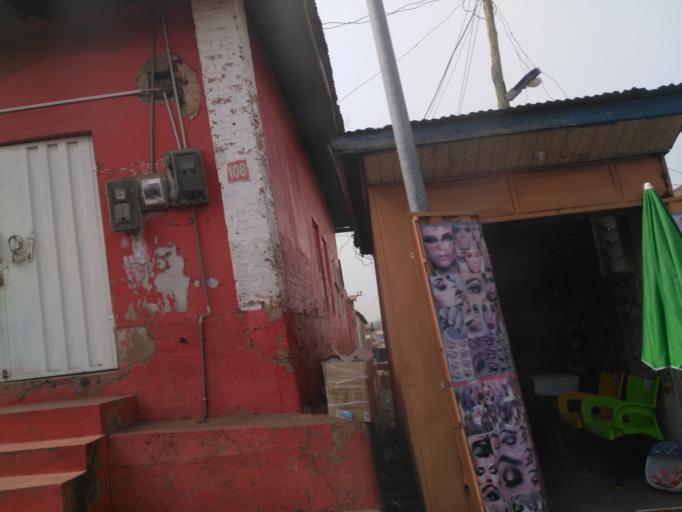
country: GH
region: Ashanti
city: Kumasi
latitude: 6.7030
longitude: -1.6183
